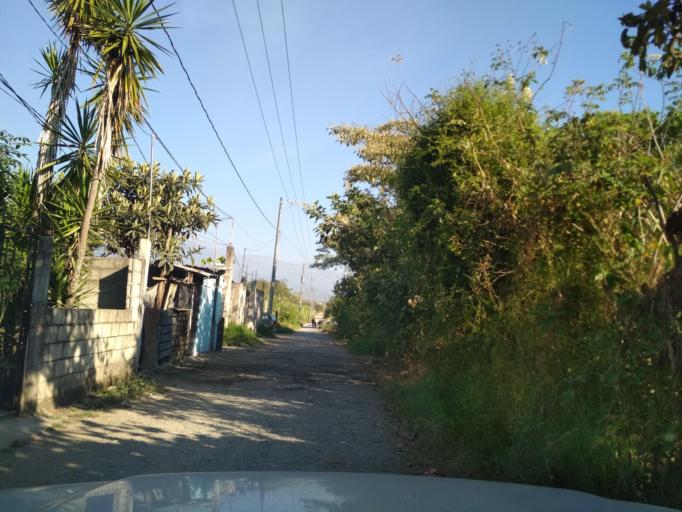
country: MX
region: Veracruz
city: Jalapilla
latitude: 18.8257
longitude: -97.0787
